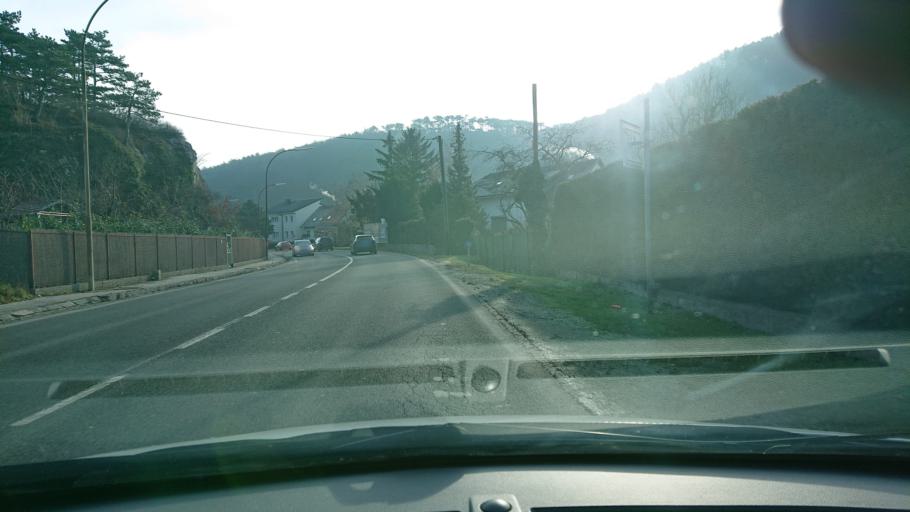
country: AT
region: Lower Austria
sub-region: Politischer Bezirk Baden
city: Hirtenberg
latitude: 47.9344
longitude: 16.1611
